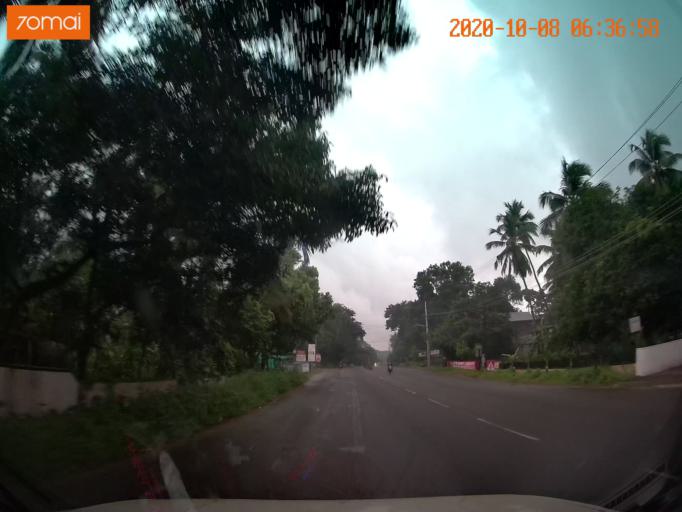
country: IN
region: Kerala
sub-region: Thrissur District
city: Avanoor
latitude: 10.6039
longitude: 76.1438
